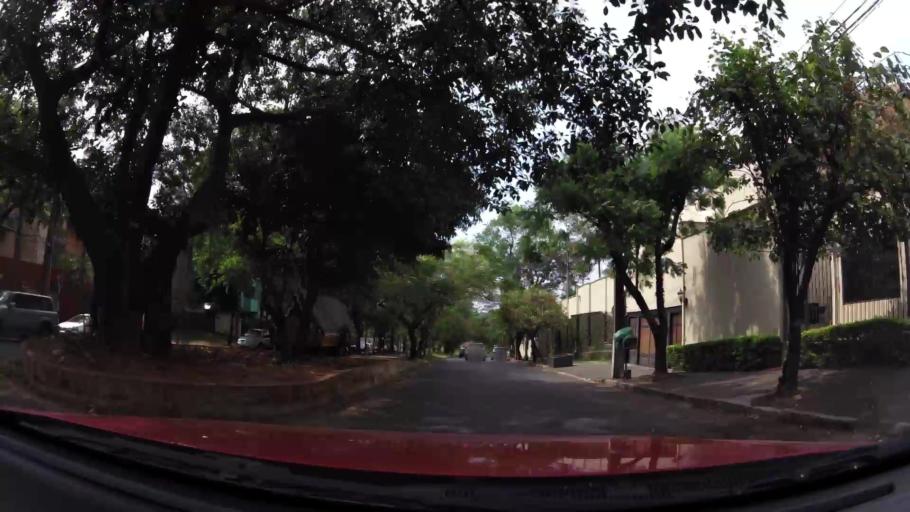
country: PY
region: Asuncion
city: Asuncion
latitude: -25.2824
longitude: -57.5800
